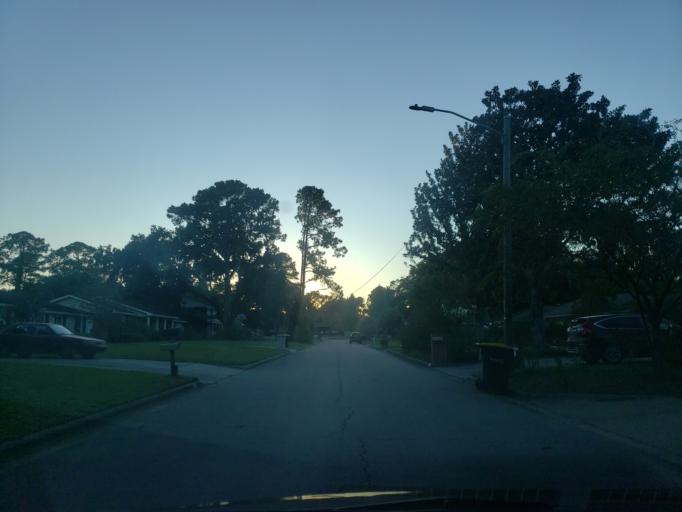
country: US
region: Georgia
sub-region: Chatham County
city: Isle of Hope
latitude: 31.9937
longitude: -81.0917
